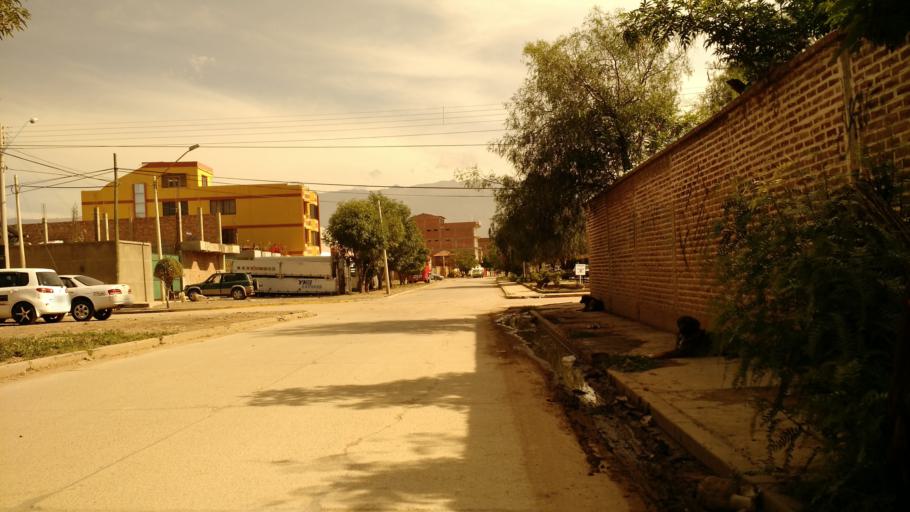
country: BO
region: Cochabamba
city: Cochabamba
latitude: -17.4339
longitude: -66.1597
